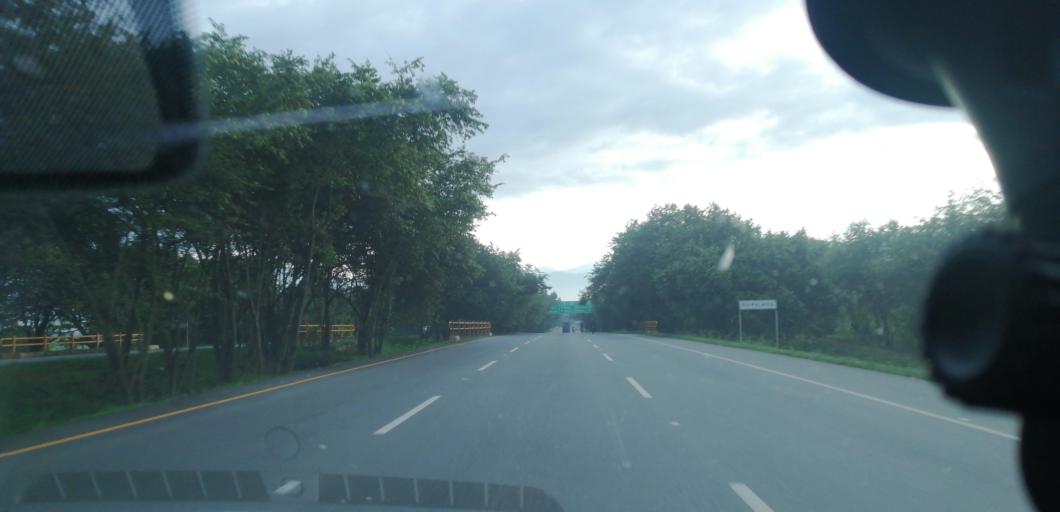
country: CO
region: Valle del Cauca
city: Palmira
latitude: 3.5216
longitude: -76.3506
